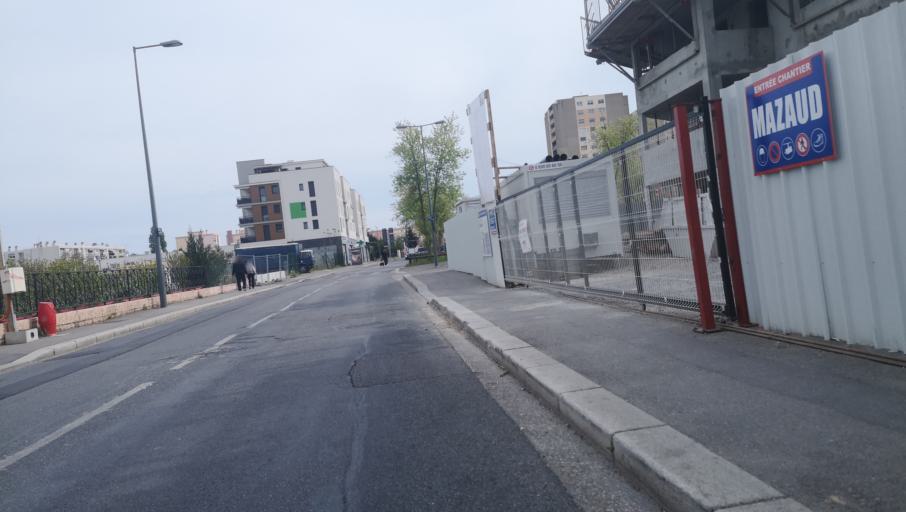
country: FR
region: Rhone-Alpes
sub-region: Departement du Rhone
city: Bron
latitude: 45.7446
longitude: 4.9190
